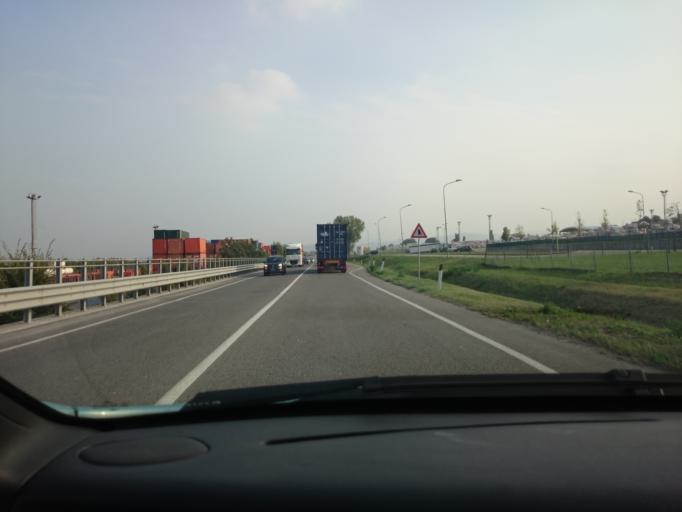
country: IT
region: Emilia-Romagna
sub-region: Provincia di Reggio Emilia
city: Veggia-Villalunga
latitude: 44.5690
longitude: 10.7530
